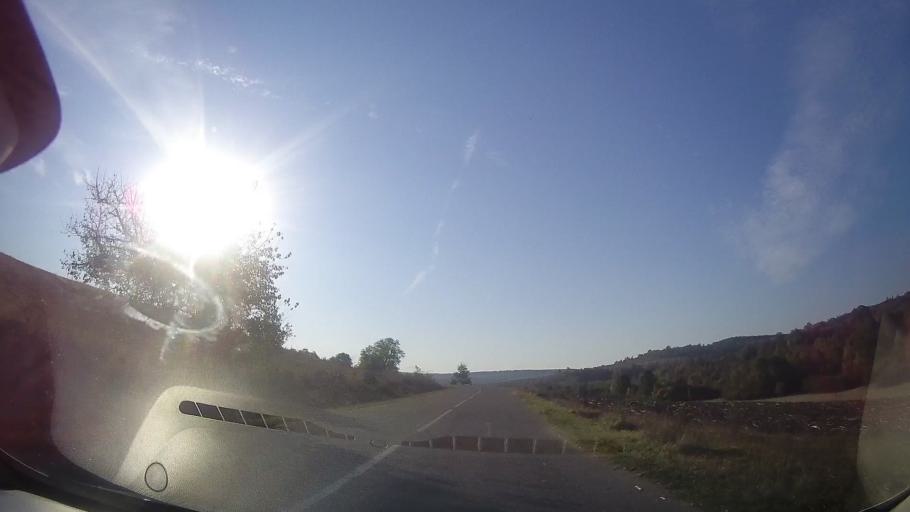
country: RO
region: Timis
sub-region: Comuna Bogda
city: Bogda
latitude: 45.9720
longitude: 21.6021
